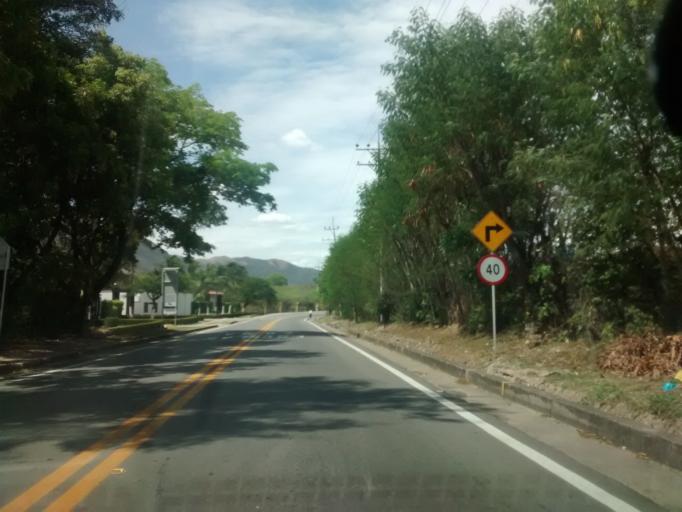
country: CO
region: Cundinamarca
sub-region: Girardot
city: Girardot City
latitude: 4.3449
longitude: -74.8037
